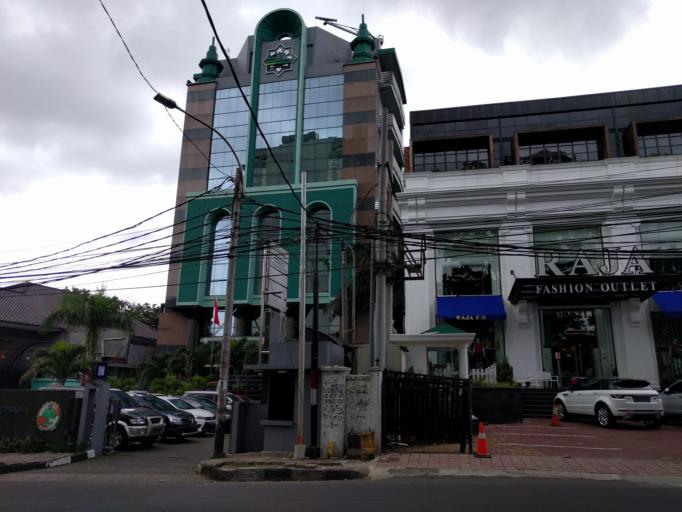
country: ID
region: West Java
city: Bogor
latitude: -6.5893
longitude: 106.8049
